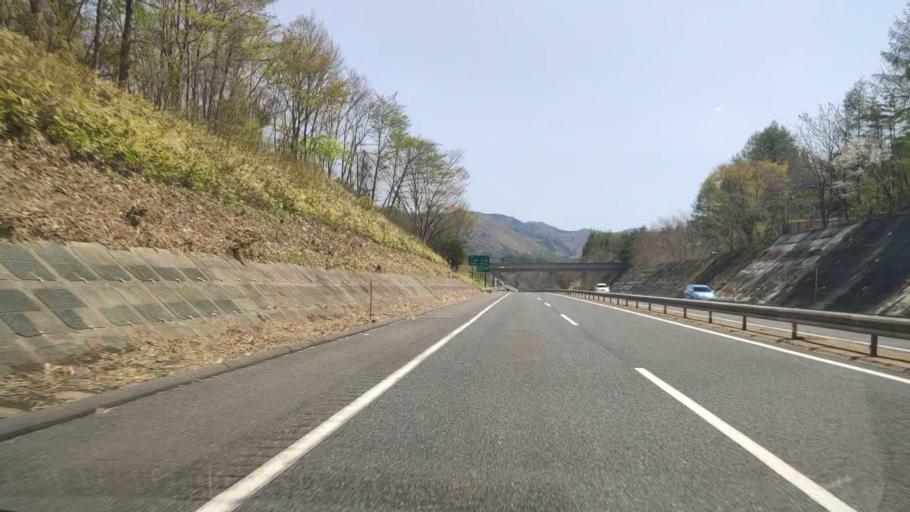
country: JP
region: Iwate
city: Ichinohe
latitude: 40.2279
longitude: 141.2770
